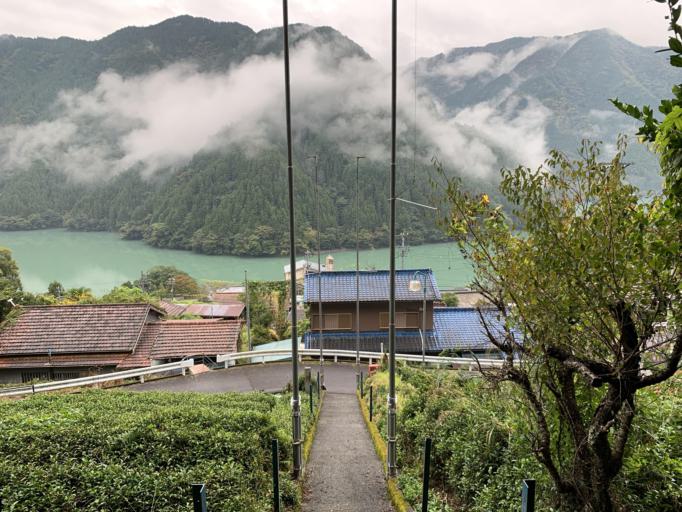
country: JP
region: Nagano
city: Iida
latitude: 35.1912
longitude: 137.8072
